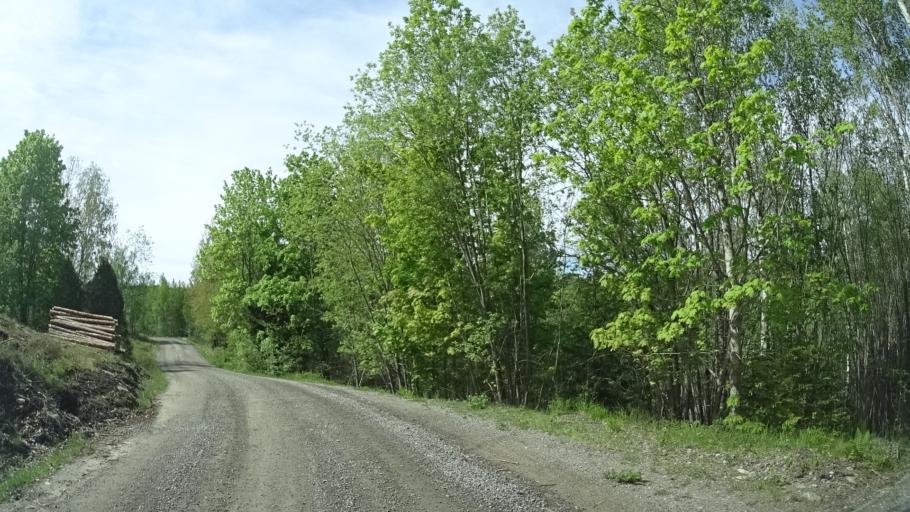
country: SE
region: OEstergoetland
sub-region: Finspangs Kommun
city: Finspang
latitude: 58.7543
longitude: 15.8311
